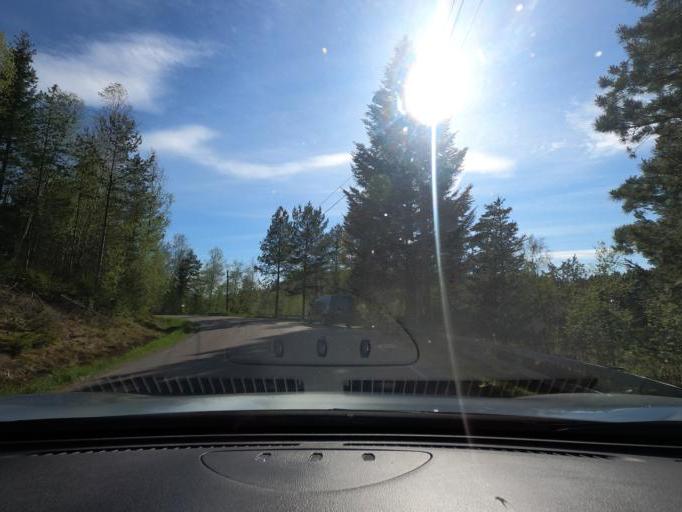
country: SE
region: Vaestra Goetaland
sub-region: Harryda Kommun
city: Hindas
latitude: 57.6448
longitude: 12.3528
